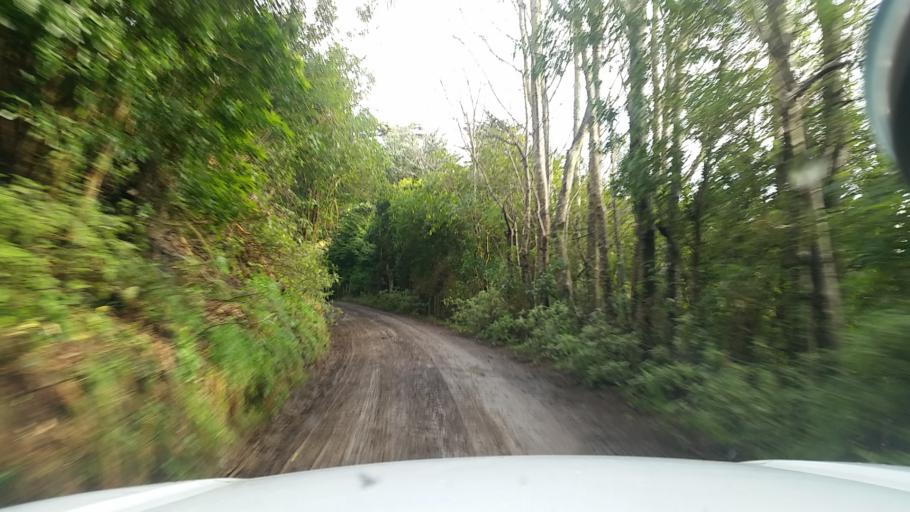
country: NZ
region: Canterbury
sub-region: Christchurch City
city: Christchurch
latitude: -43.7343
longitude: 172.8858
